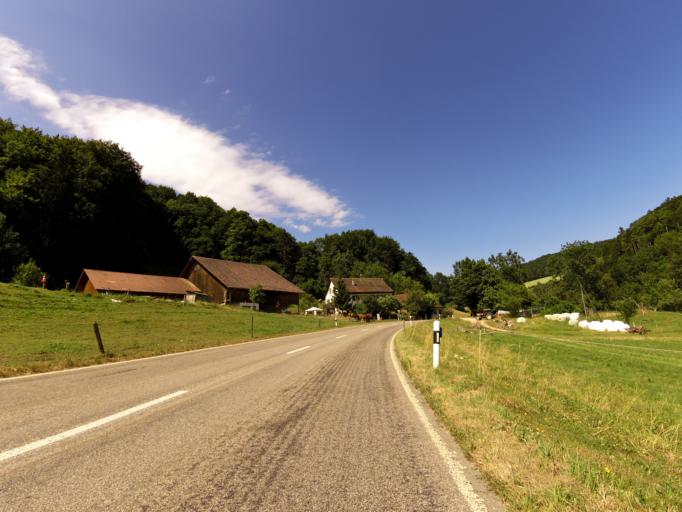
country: CH
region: Basel-Landschaft
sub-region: Bezirk Waldenburg
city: Langenbruck
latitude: 47.3409
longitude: 7.7678
